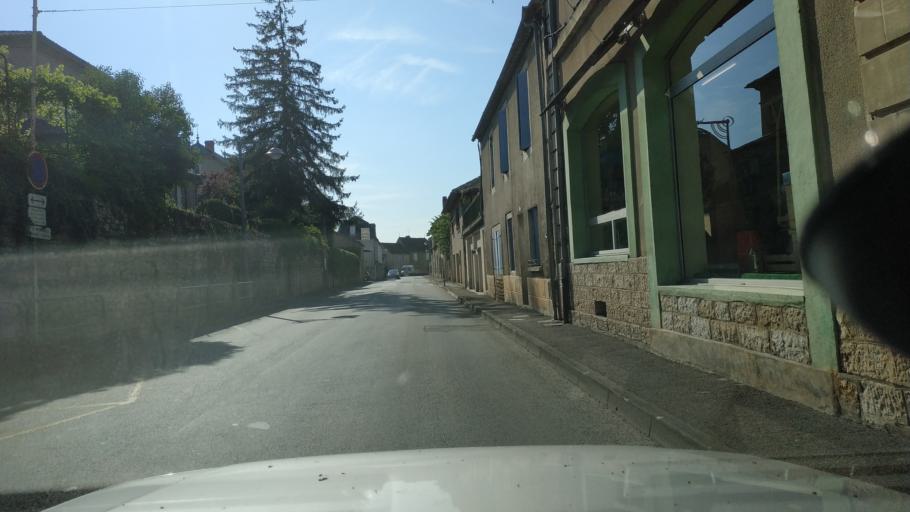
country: FR
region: Midi-Pyrenees
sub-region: Departement du Lot
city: Gramat
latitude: 44.7806
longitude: 1.7232
